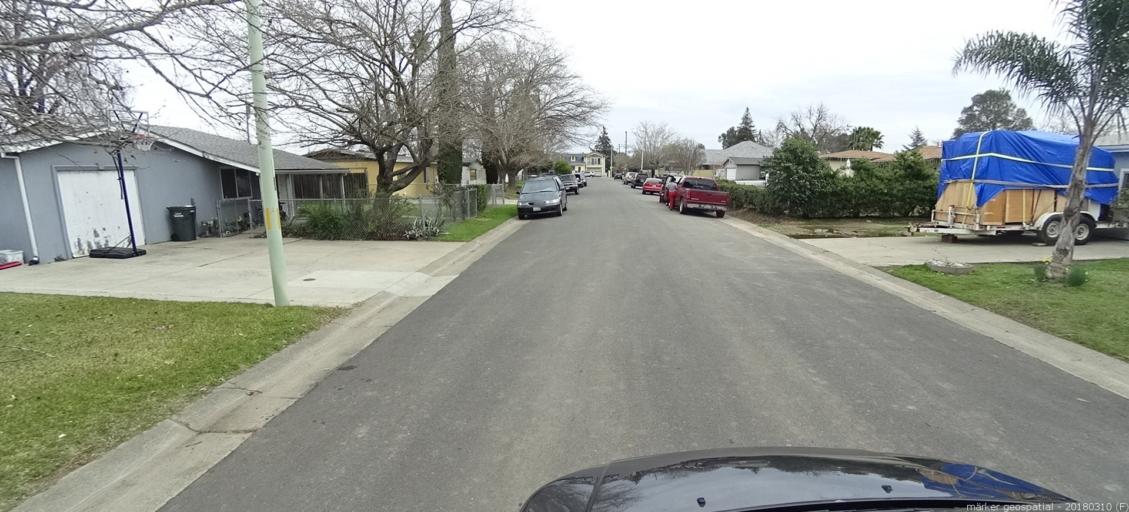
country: US
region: California
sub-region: Sacramento County
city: Florin
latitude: 38.4948
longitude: -121.4058
